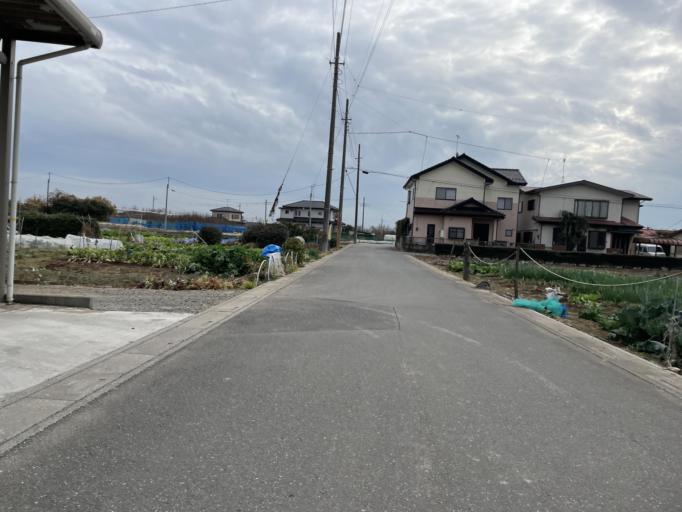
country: JP
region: Saitama
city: Shiraoka
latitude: 36.0203
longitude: 139.6439
